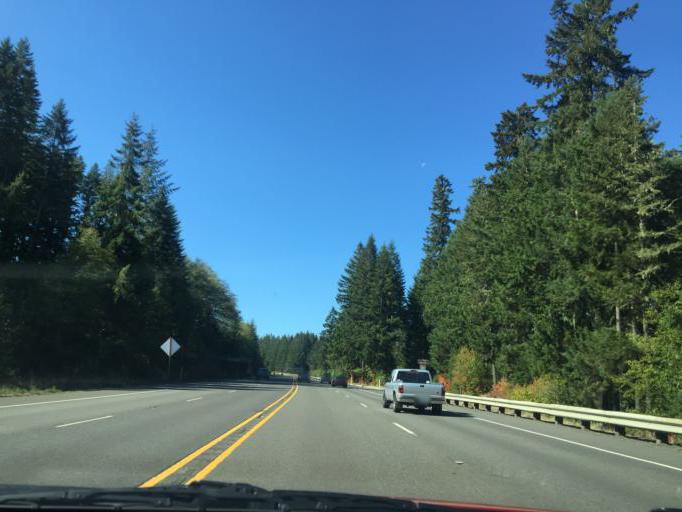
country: US
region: Oregon
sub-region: Columbia County
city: Vernonia
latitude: 45.7805
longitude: -123.3501
